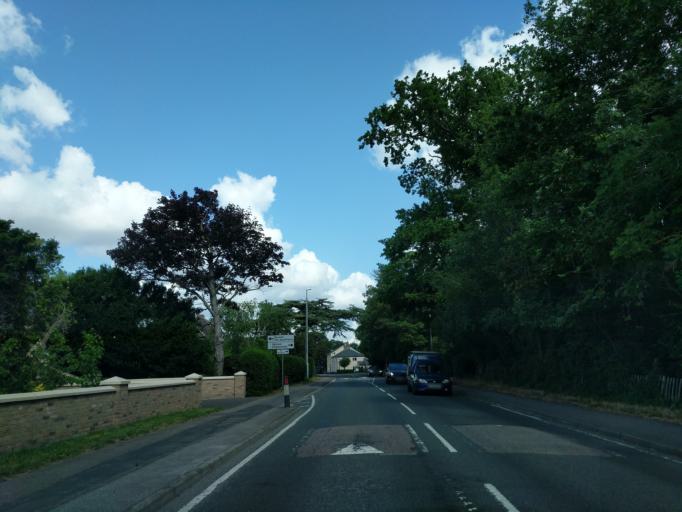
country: GB
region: England
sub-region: Suffolk
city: Exning
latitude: 52.3048
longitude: 0.3860
